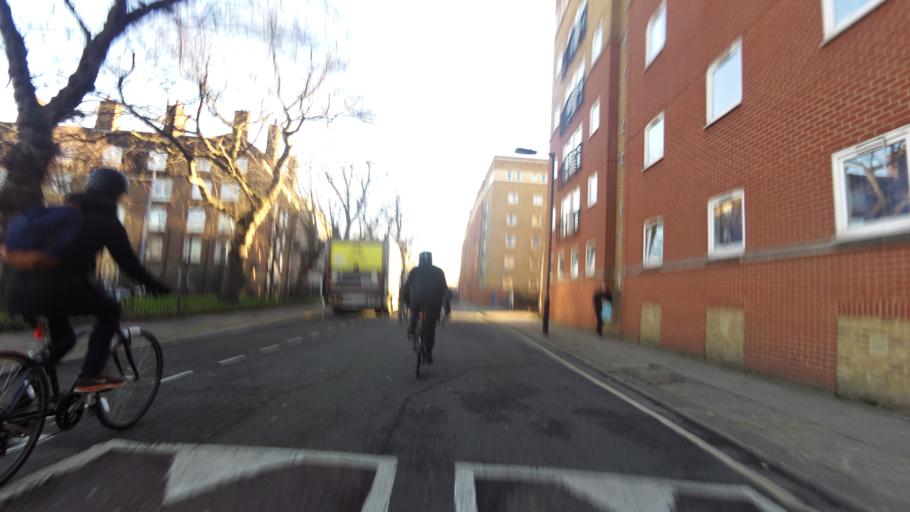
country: GB
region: England
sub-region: Greater London
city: City of London
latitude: 51.4978
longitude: -0.0890
